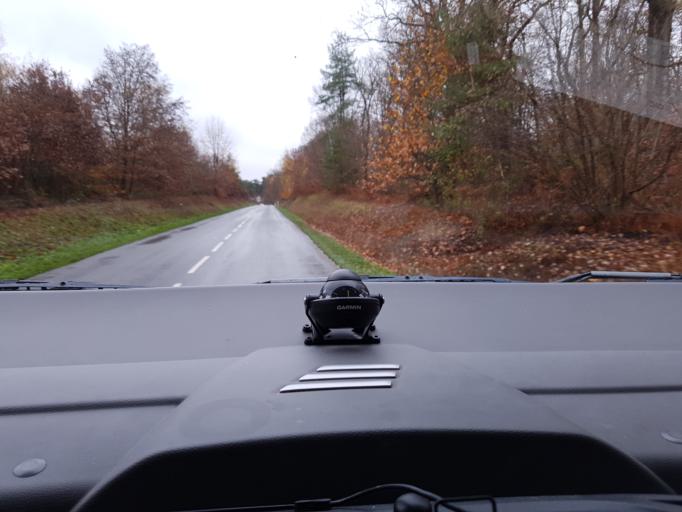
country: FR
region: Haute-Normandie
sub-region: Departement de l'Eure
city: Pont-Saint-Pierre
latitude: 49.3240
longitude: 1.2926
